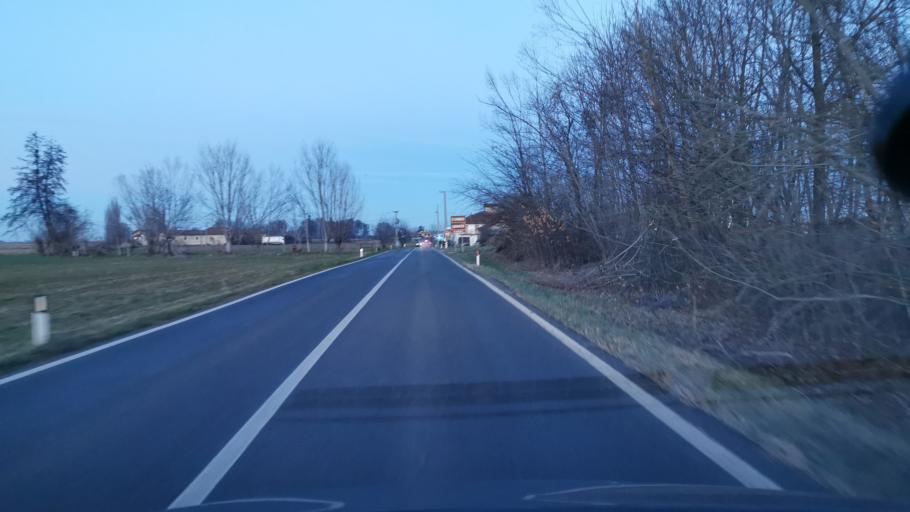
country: IT
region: Piedmont
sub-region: Provincia di Cuneo
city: Roata Rossi
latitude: 44.4502
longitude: 7.4793
